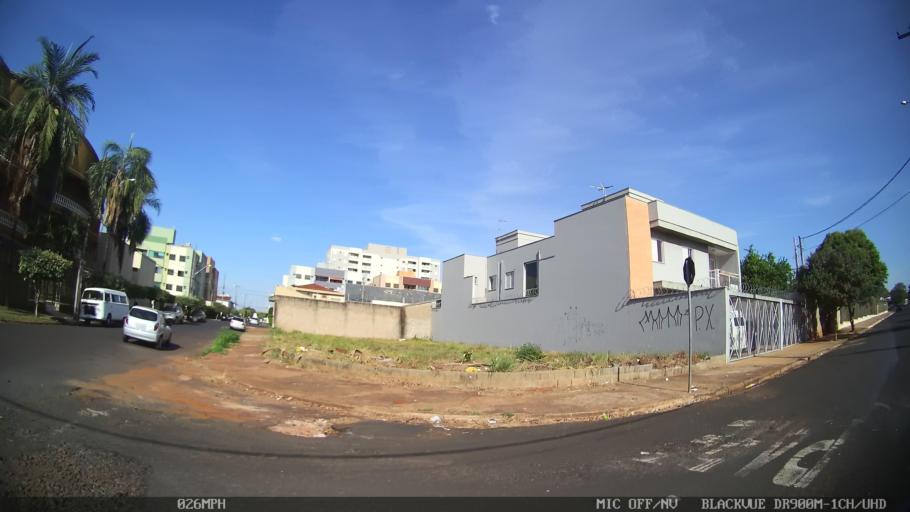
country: BR
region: Sao Paulo
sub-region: Ribeirao Preto
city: Ribeirao Preto
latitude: -21.1749
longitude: -47.7600
